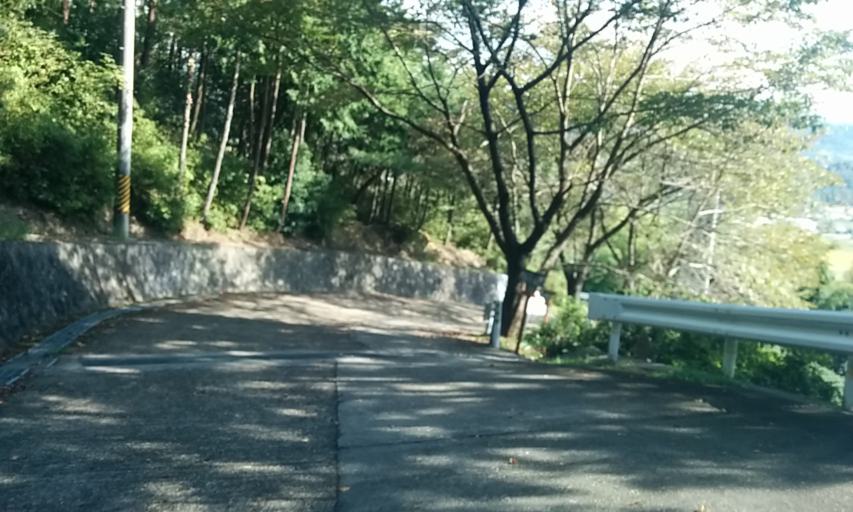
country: JP
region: Nara
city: Nara-shi
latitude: 34.7735
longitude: 135.8638
